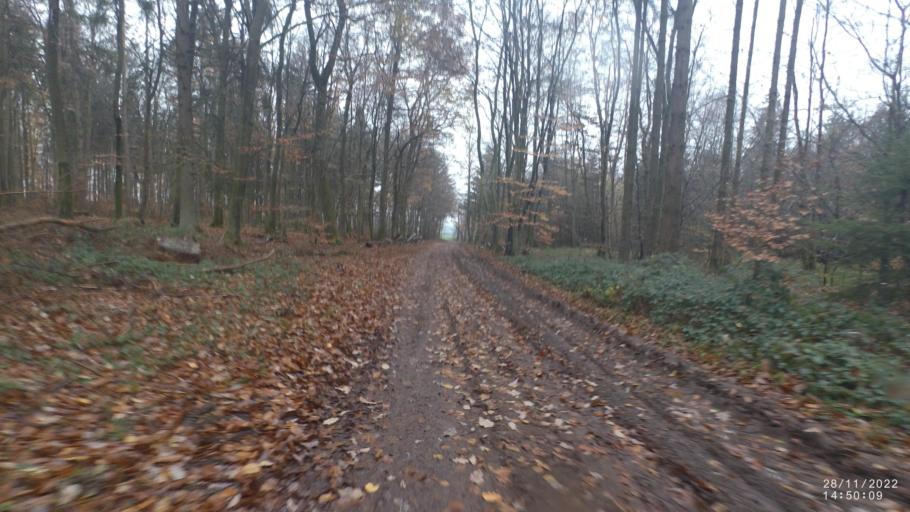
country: DE
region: Rheinland-Pfalz
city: Oberehe-Stroheich
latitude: 50.2964
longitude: 6.7545
